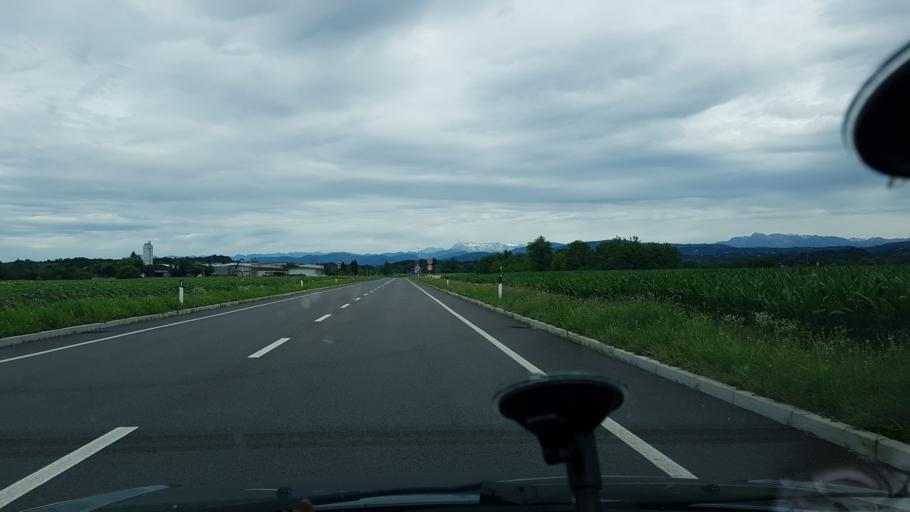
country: IT
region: Friuli Venezia Giulia
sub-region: Provincia di Gorizia
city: Mossa
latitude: 45.9265
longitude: 13.5548
